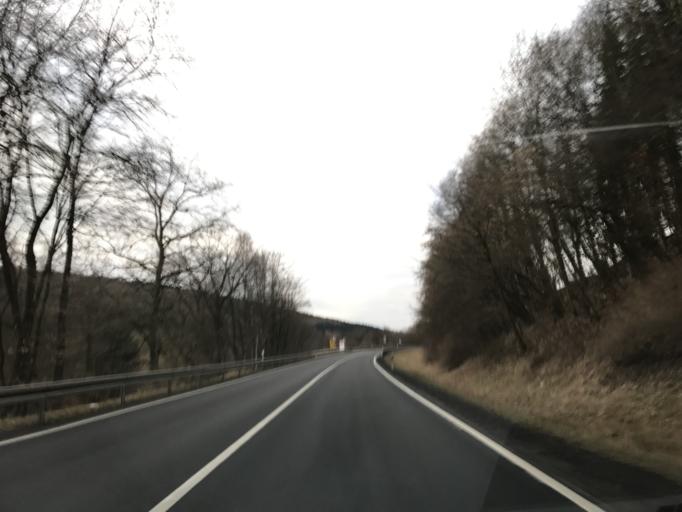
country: DE
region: Hesse
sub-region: Regierungsbezirk Kassel
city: Helsa
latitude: 51.2470
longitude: 9.6833
